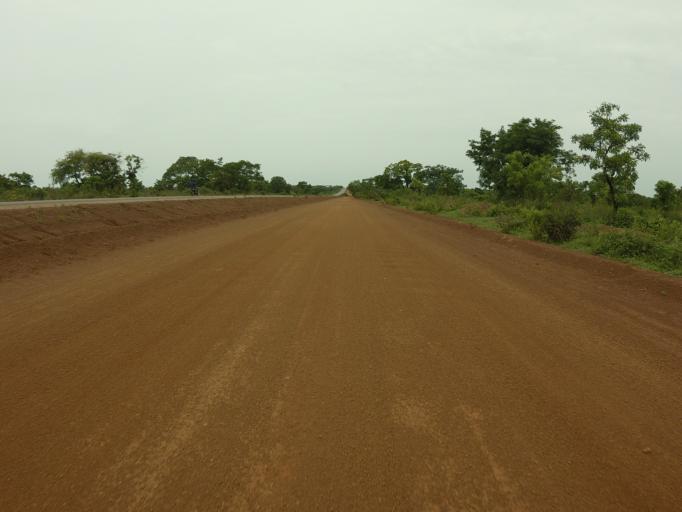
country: GH
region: Northern
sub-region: Yendi
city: Yendi
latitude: 9.0272
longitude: -0.0137
